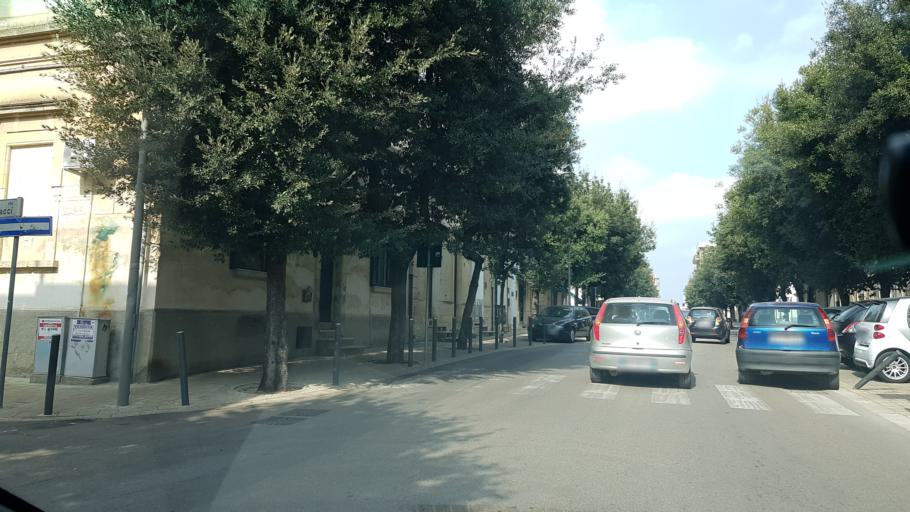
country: IT
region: Apulia
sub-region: Provincia di Lecce
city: Castromediano
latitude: 40.3402
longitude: 18.1764
